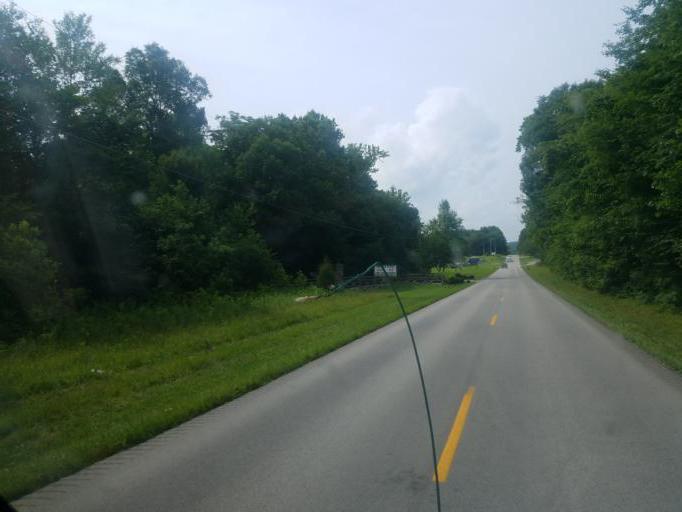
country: US
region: Kentucky
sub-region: Edmonson County
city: Brownsville
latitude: 37.3322
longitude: -86.1242
